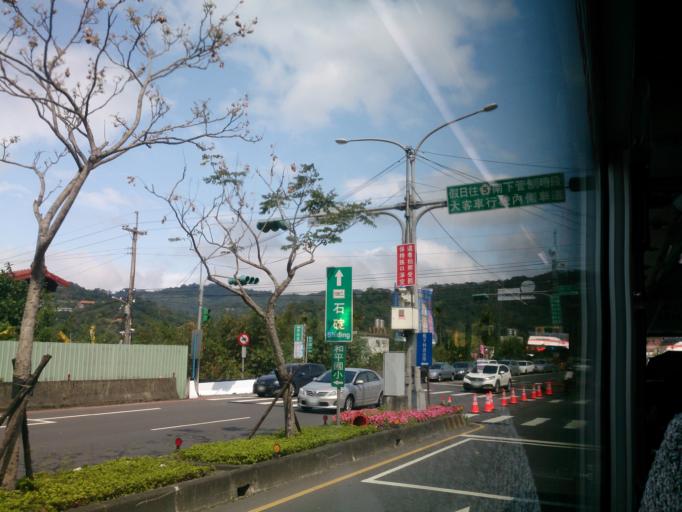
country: TW
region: Taipei
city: Taipei
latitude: 25.0087
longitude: 121.6422
